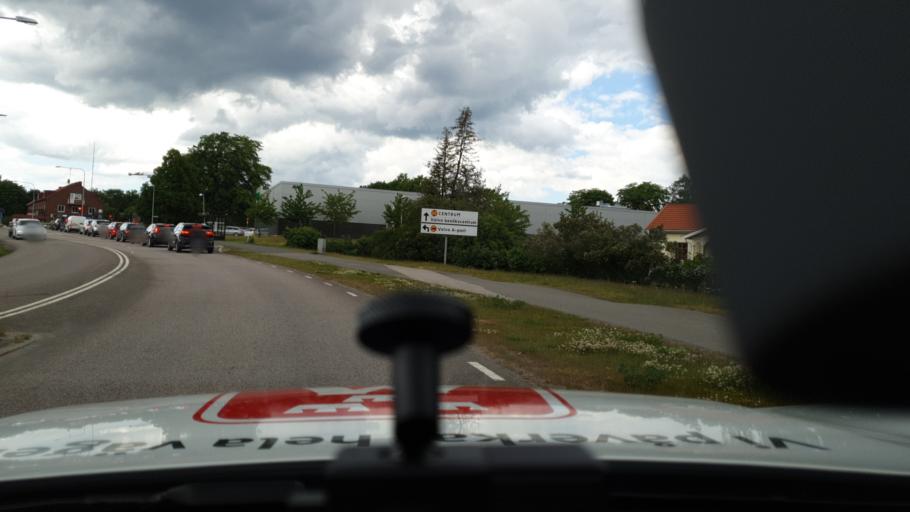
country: SE
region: Vaestra Goetaland
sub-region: Skovde Kommun
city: Skoevde
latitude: 58.3860
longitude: 13.8605
